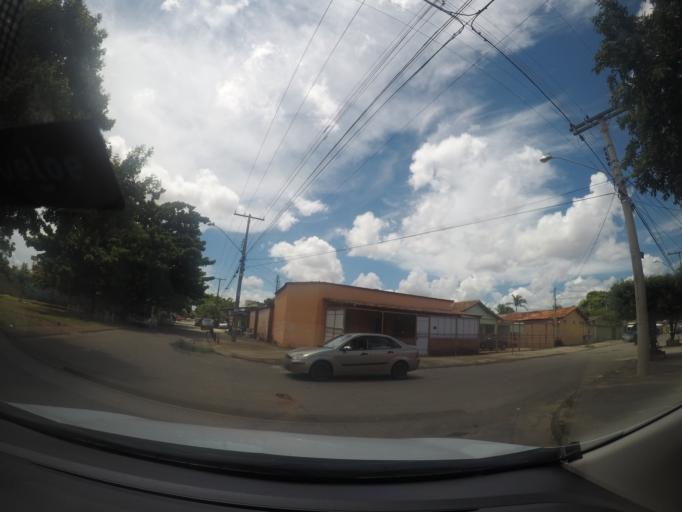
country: BR
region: Goias
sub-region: Goiania
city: Goiania
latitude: -16.6762
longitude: -49.3129
